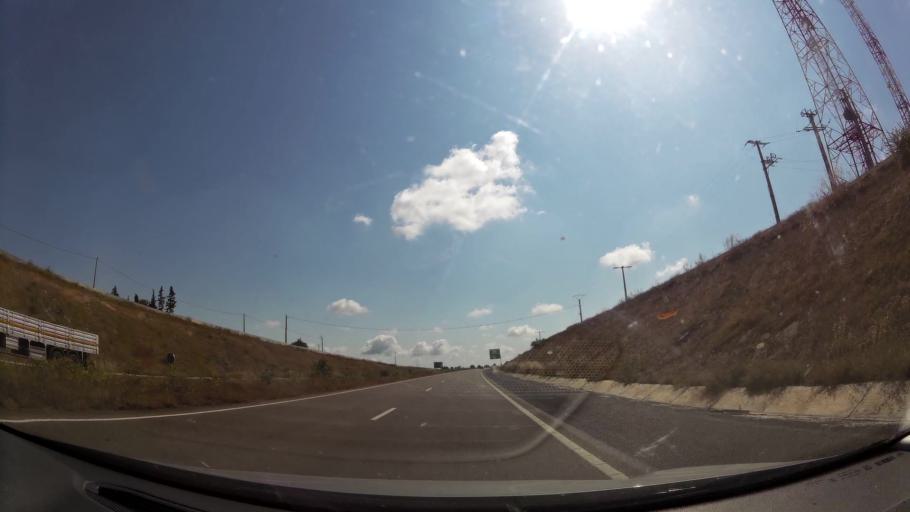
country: MA
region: Rabat-Sale-Zemmour-Zaer
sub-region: Skhirate-Temara
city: Temara
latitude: 33.8491
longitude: -6.8322
